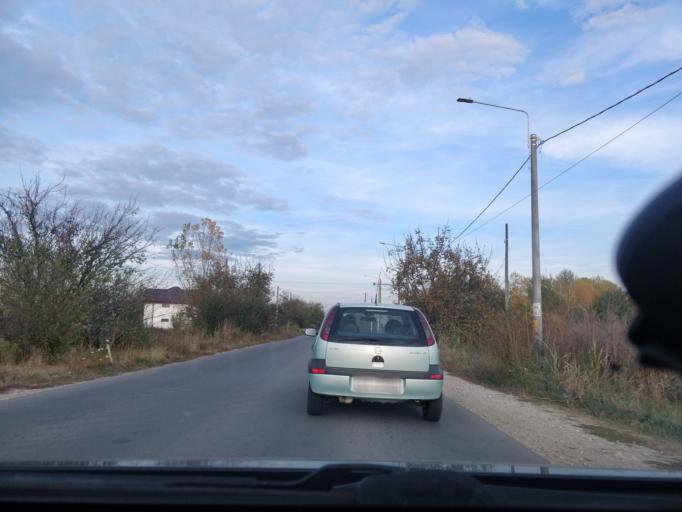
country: RO
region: Giurgiu
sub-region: Comuna Bolintin Vale
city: Malu Spart
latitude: 44.4409
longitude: 25.7350
